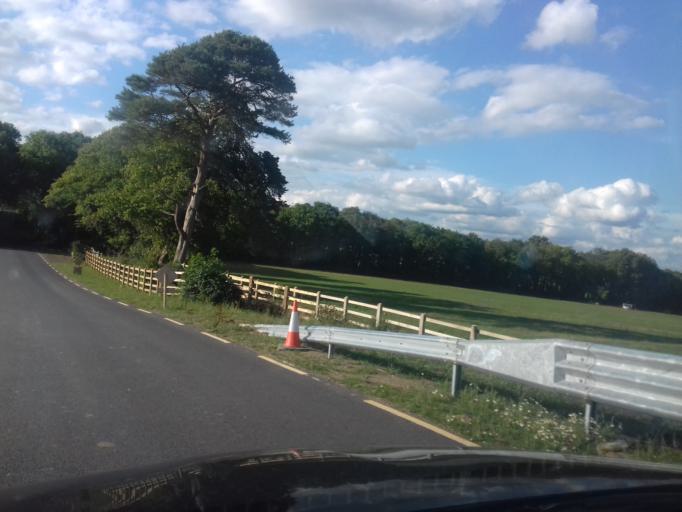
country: IE
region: Leinster
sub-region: Loch Garman
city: New Ross
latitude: 52.3743
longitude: -6.9211
